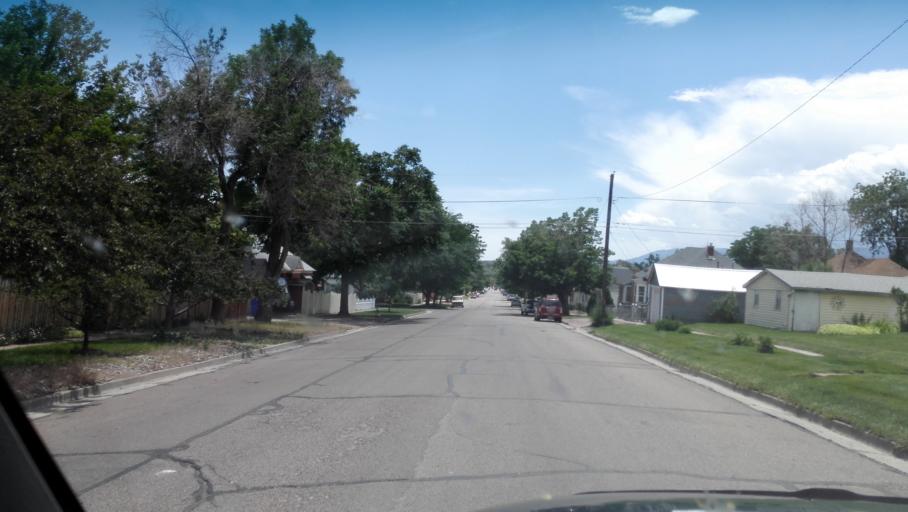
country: US
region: Colorado
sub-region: Fremont County
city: Canon City
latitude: 38.4461
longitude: -105.2450
